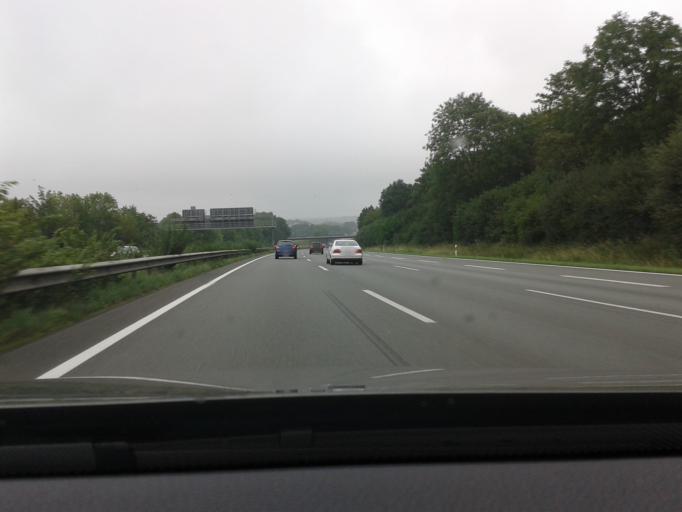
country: DE
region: North Rhine-Westphalia
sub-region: Regierungsbezirk Detmold
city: Oerlinghausen
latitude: 52.0000
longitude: 8.6206
